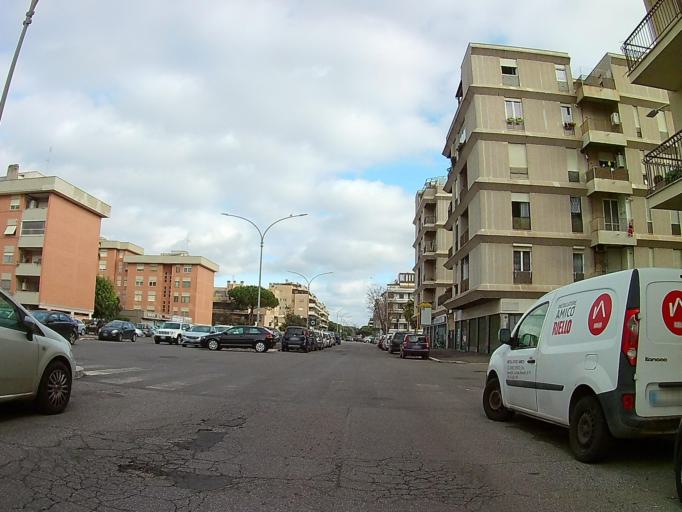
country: IT
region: Latium
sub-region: Citta metropolitana di Roma Capitale
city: Lido di Ostia
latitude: 41.7400
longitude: 12.2666
